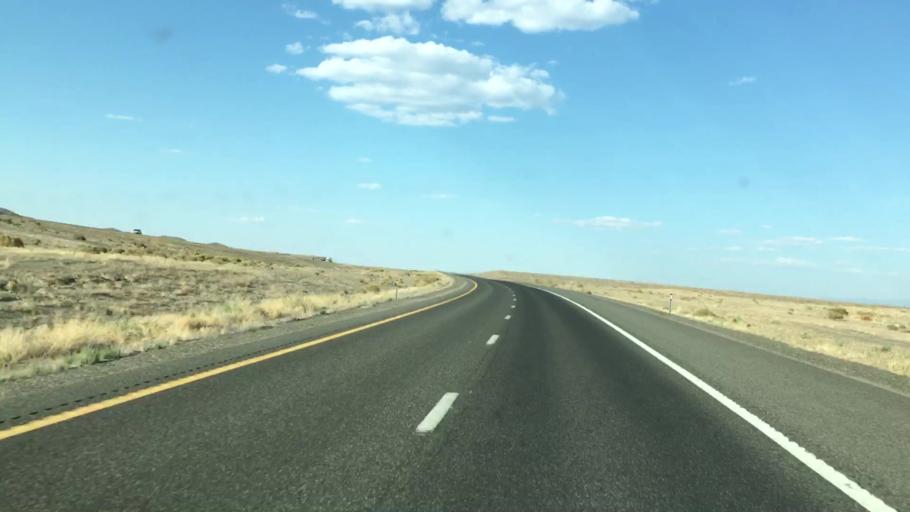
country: US
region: Nevada
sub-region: Pershing County
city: Lovelock
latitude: 39.9612
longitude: -118.7045
